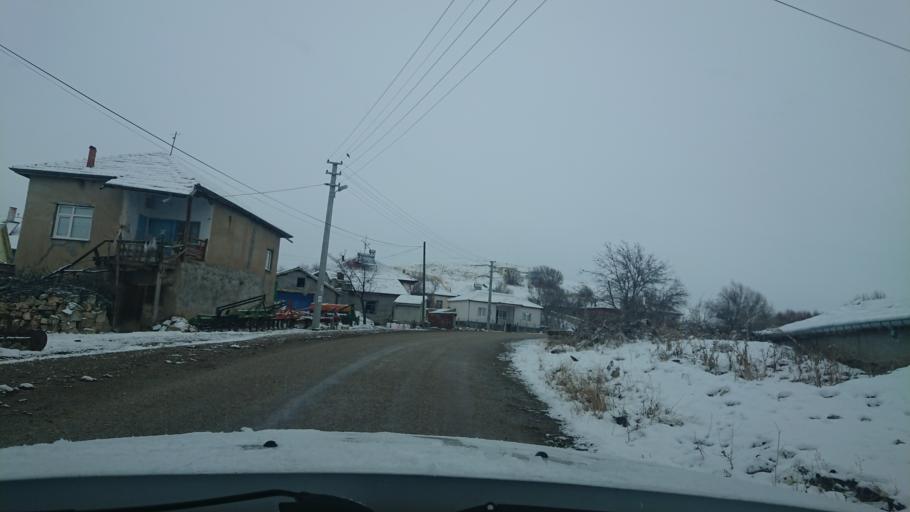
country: TR
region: Aksaray
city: Agacoren
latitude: 38.7585
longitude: 33.8684
